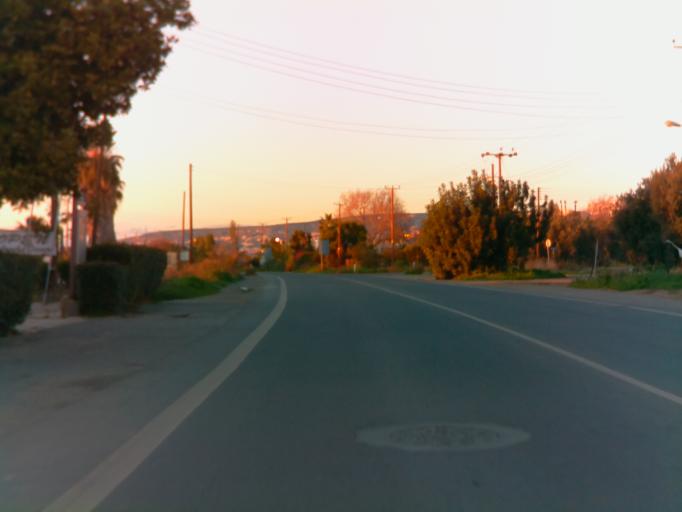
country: CY
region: Pafos
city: Chlorakas
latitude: 34.7978
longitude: 32.4008
